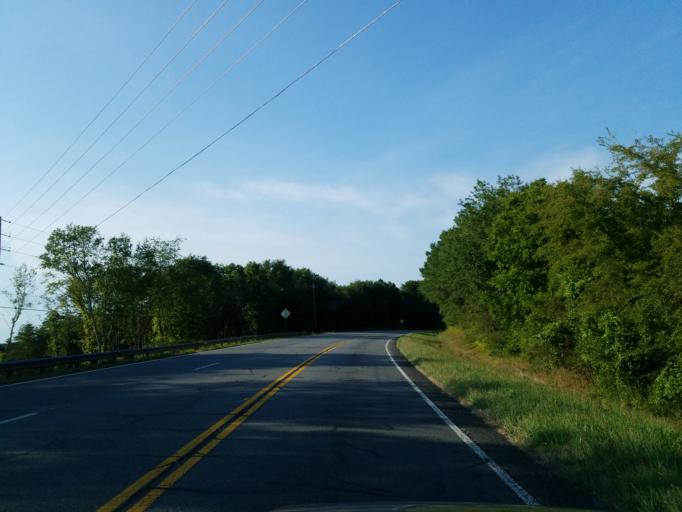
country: US
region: Georgia
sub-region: Bartow County
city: Rydal
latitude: 34.3813
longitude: -84.7094
